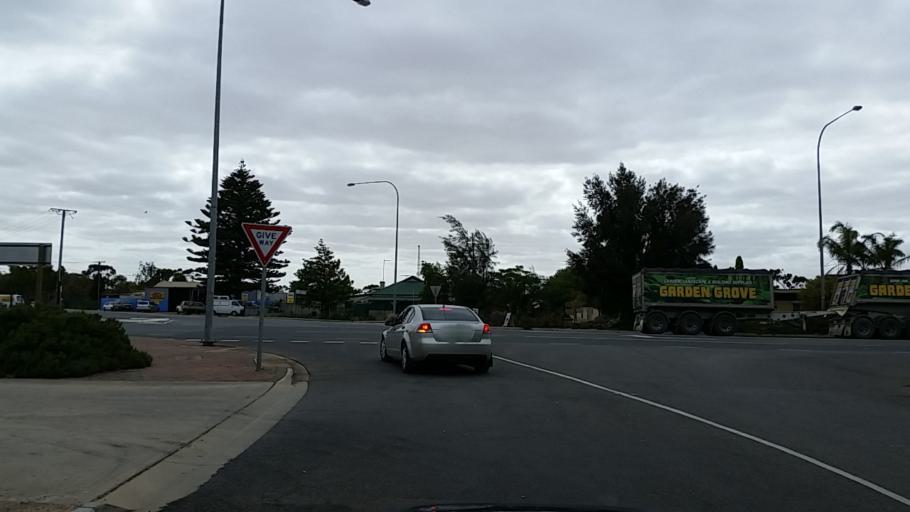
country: AU
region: South Australia
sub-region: Wakefield
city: Balaklava
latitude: -34.1840
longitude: 138.1532
